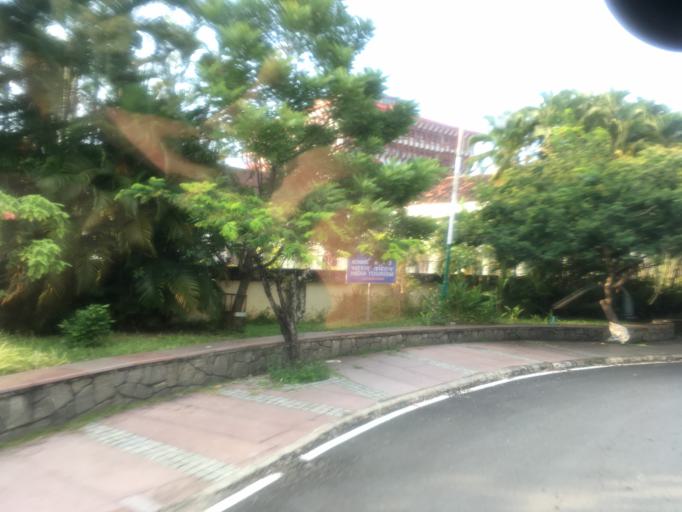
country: IN
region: Kerala
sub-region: Ernakulam
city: Cochin
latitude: 9.9693
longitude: 76.2590
